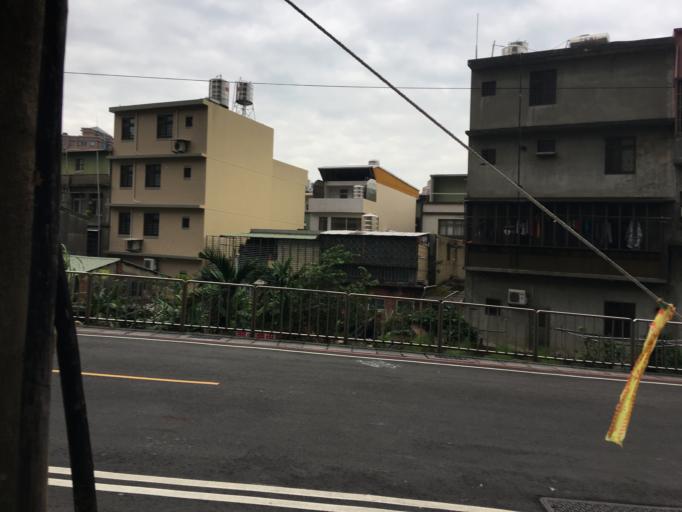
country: TW
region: Taiwan
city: Taoyuan City
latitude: 25.0180
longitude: 121.3058
